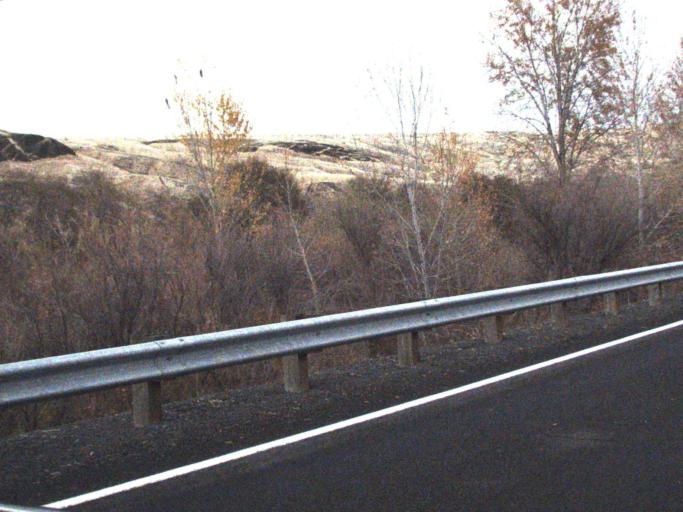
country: US
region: Washington
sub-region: Walla Walla County
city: Waitsburg
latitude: 46.5441
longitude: -118.1645
